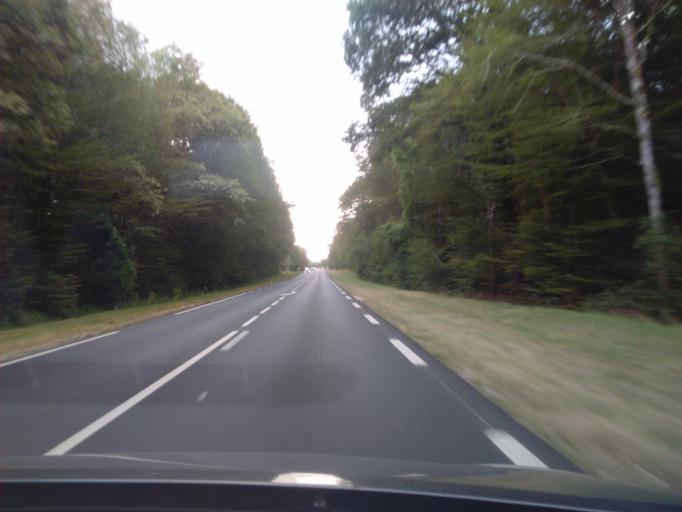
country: FR
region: Centre
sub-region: Departement du Loir-et-Cher
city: Cellettes
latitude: 47.5409
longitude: 1.3750
